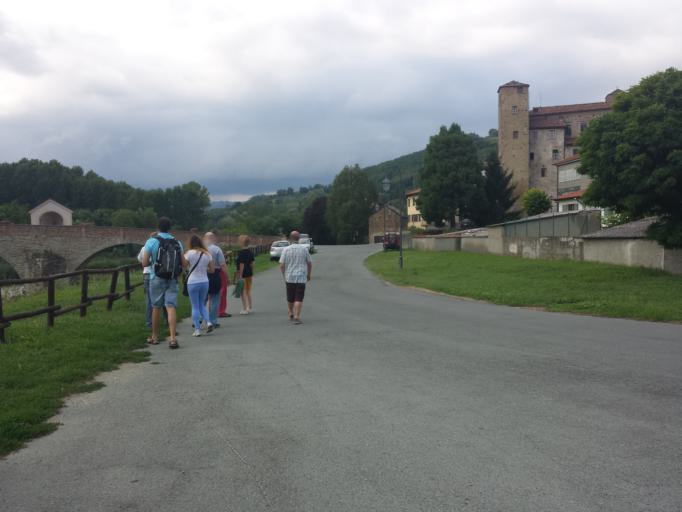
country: IT
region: Piedmont
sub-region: Provincia di Asti
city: Monastero Bormida
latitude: 44.6463
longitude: 8.3248
